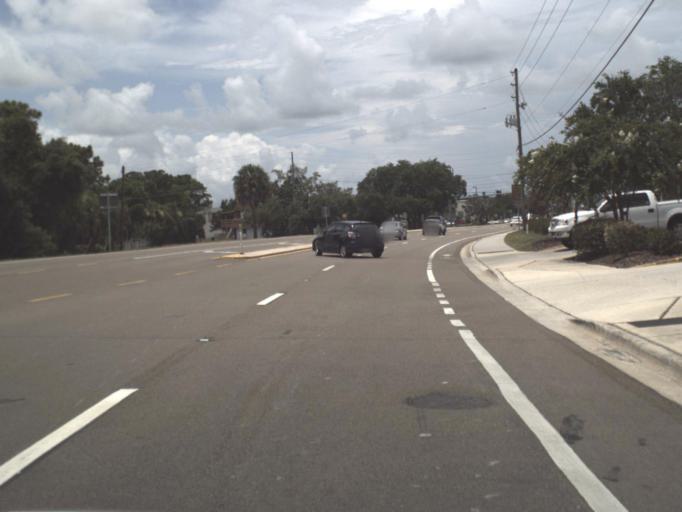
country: US
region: Florida
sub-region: Pinellas County
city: Dunedin
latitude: 28.0490
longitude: -82.7780
